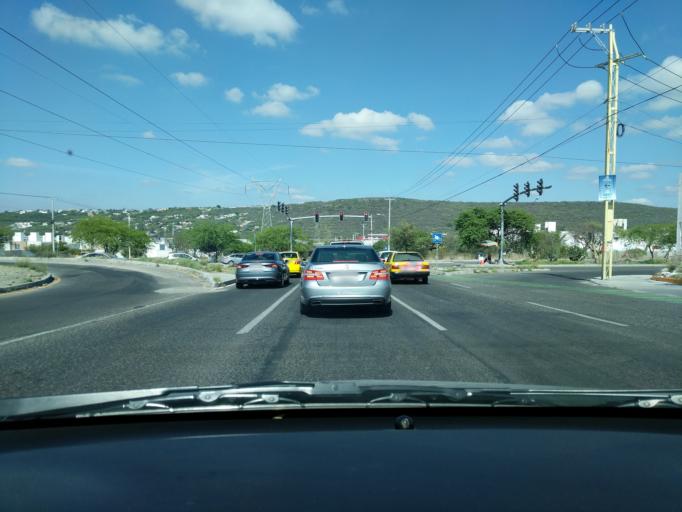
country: MX
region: Queretaro
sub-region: Queretaro
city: Patria Nueva
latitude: 20.6425
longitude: -100.4915
